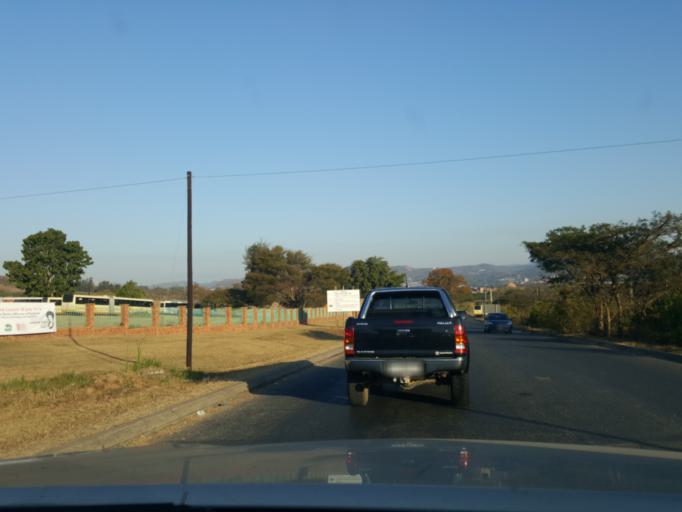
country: ZA
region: Mpumalanga
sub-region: Ehlanzeni District
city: Nelspruit
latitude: -25.4273
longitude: 30.9669
